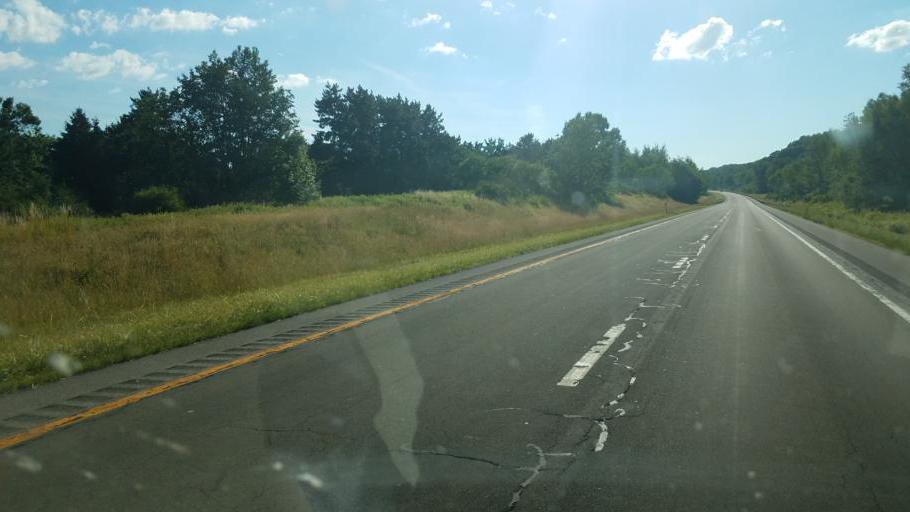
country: US
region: New York
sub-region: Chautauqua County
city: Falconer
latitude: 42.1367
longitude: -79.1528
